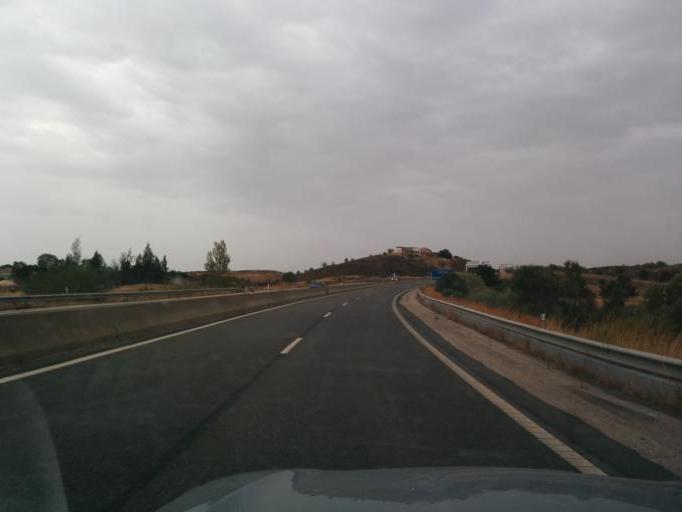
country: PT
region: Faro
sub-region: Castro Marim
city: Castro Marim
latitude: 37.2339
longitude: -7.4443
